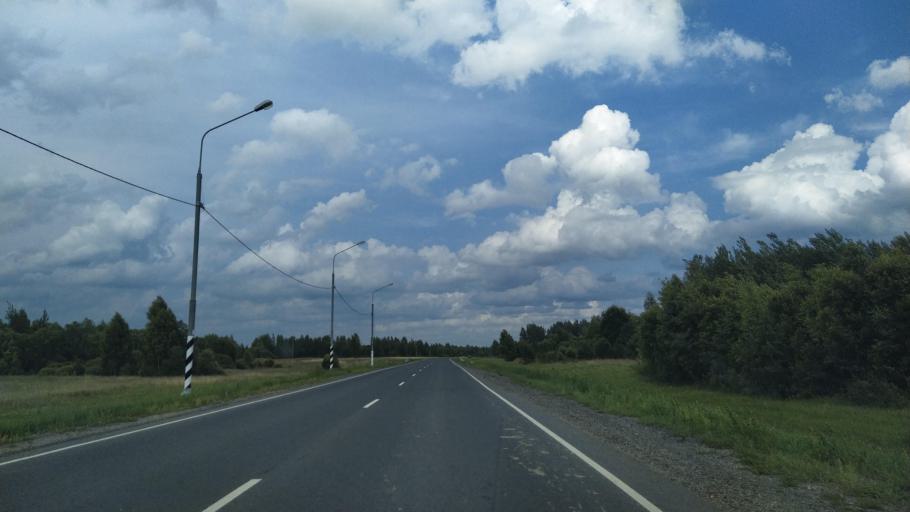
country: RU
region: Pskov
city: Dno
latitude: 58.0638
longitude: 30.0307
